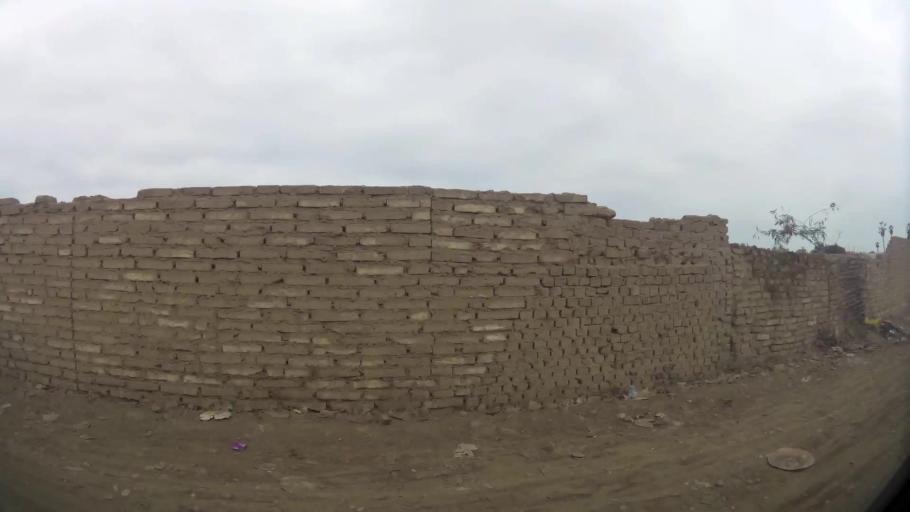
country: PE
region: Lima
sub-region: Provincia de Huaral
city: Huaral
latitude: -11.4861
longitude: -77.2097
